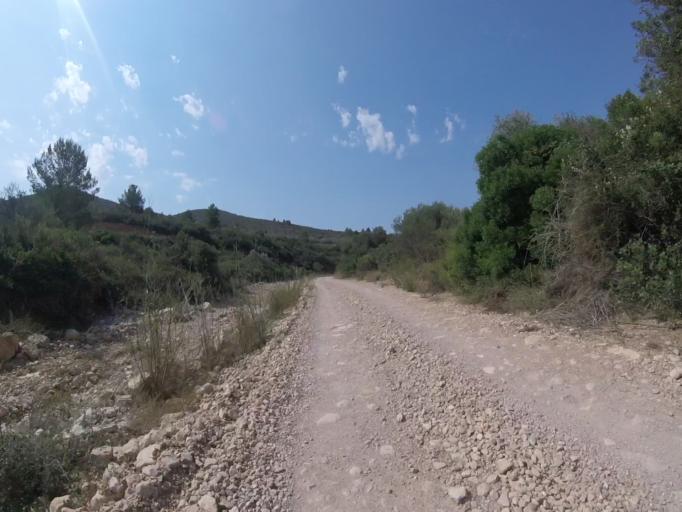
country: ES
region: Valencia
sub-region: Provincia de Castello
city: Cuevas de Vinroma
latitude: 40.3096
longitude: 0.1764
